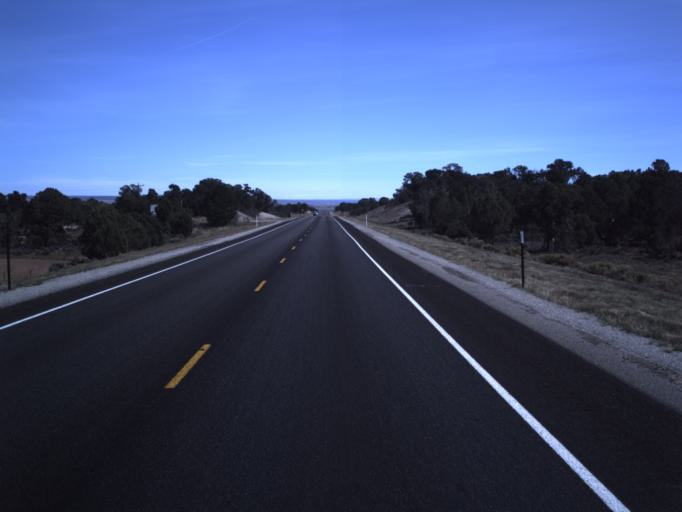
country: US
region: Colorado
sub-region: Dolores County
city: Dove Creek
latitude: 37.8296
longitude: -109.0876
